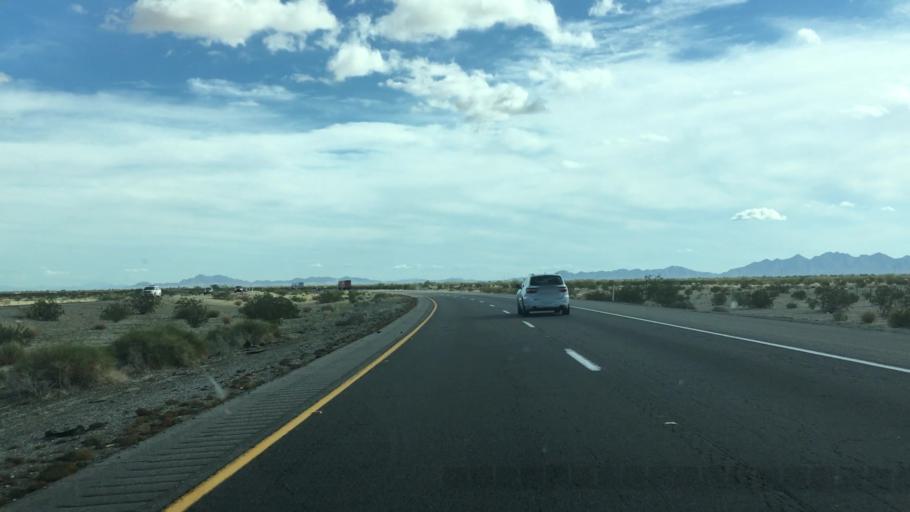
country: US
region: California
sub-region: Riverside County
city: Mesa Verde
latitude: 33.6321
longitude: -115.0768
